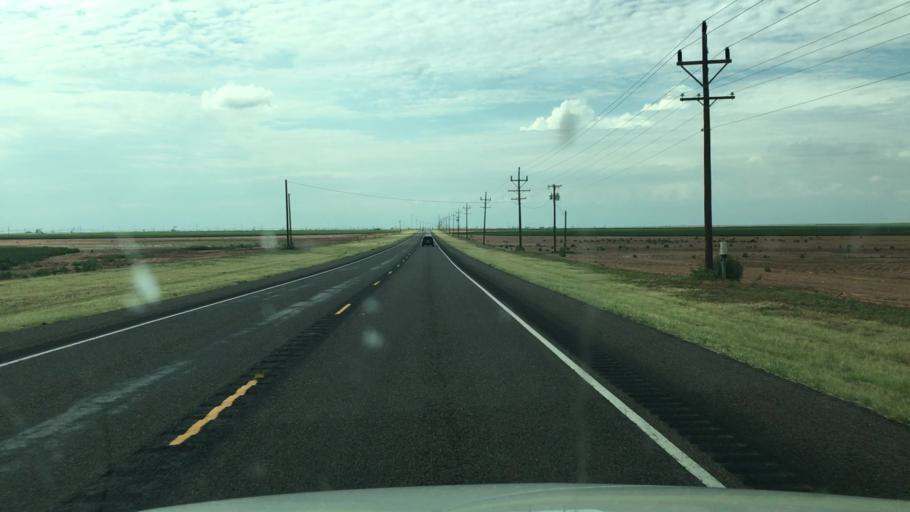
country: US
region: Texas
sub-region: Dawson County
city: Lamesa
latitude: 32.8826
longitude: -102.0824
